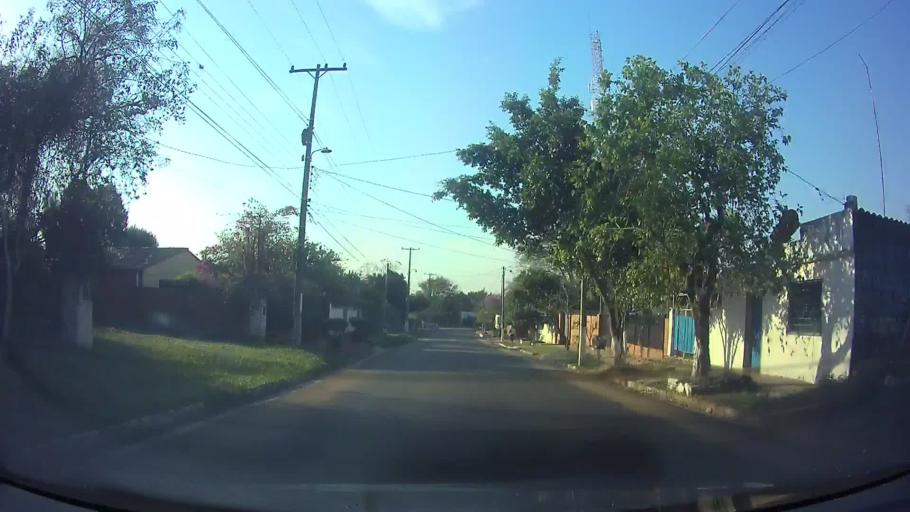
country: PY
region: Central
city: San Lorenzo
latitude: -25.2601
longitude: -57.4803
